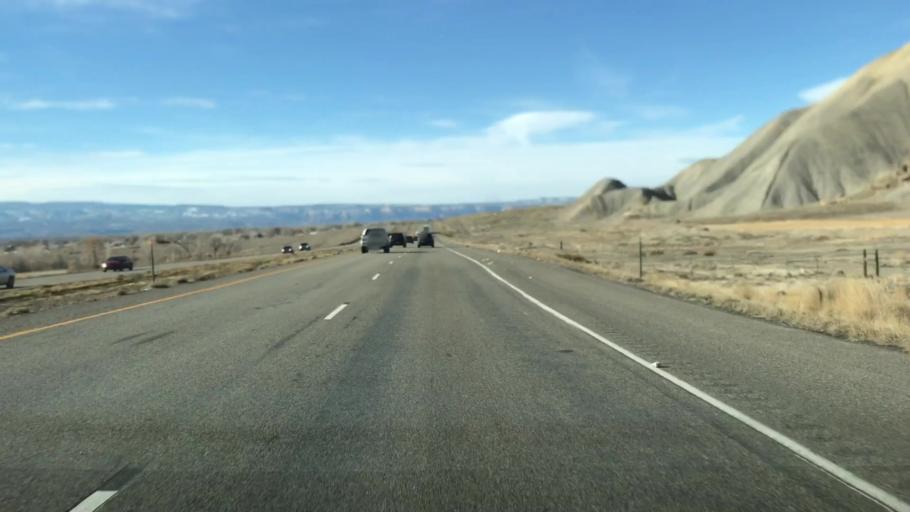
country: US
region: Colorado
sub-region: Mesa County
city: Palisade
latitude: 39.1151
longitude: -108.4007
